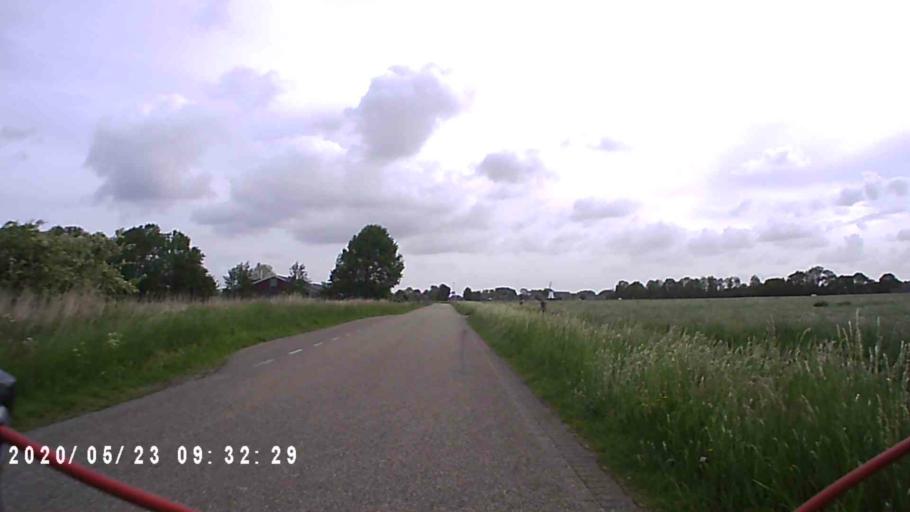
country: NL
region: Groningen
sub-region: Gemeente Slochteren
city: Slochteren
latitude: 53.2961
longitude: 6.7186
